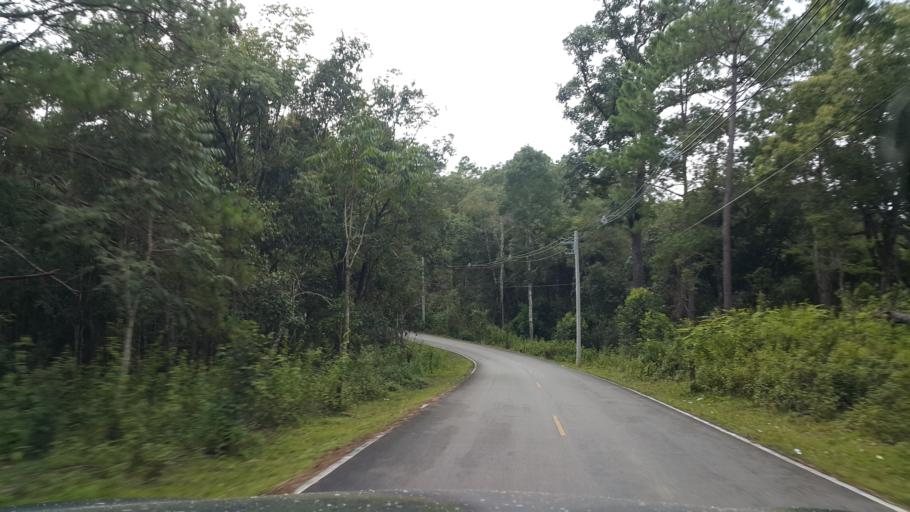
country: TH
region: Chiang Mai
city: Chaem Luang
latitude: 18.9132
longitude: 98.4975
